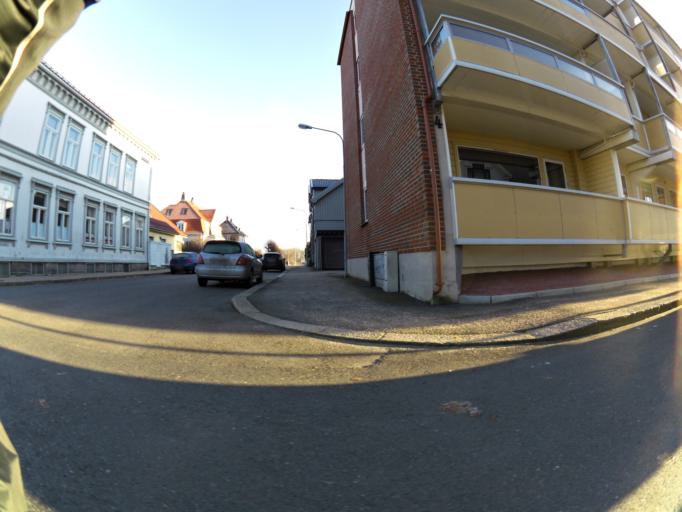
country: NO
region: Ostfold
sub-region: Fredrikstad
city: Fredrikstad
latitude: 59.2059
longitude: 10.9441
